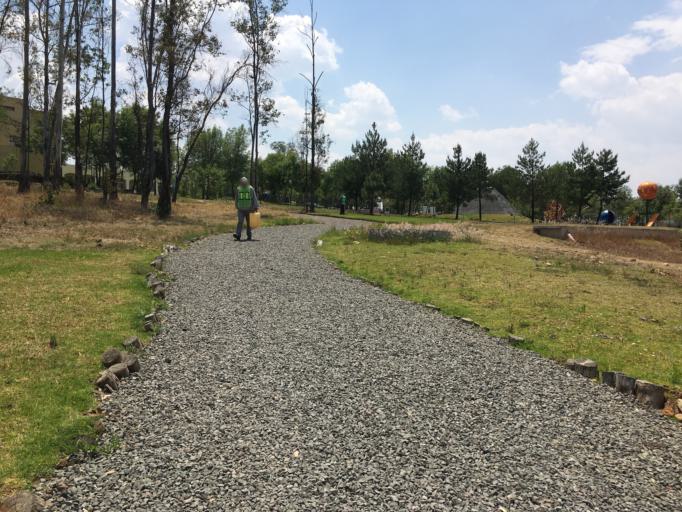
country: MX
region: Michoacan
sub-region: Morelia
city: Morelos
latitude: 19.6480
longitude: -101.2280
